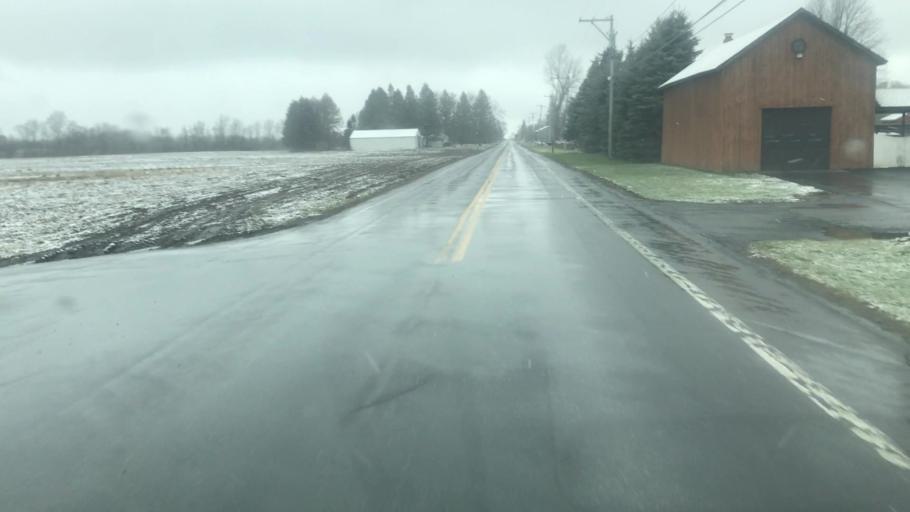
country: US
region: New York
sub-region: Onondaga County
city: Marcellus
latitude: 42.9950
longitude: -76.3882
